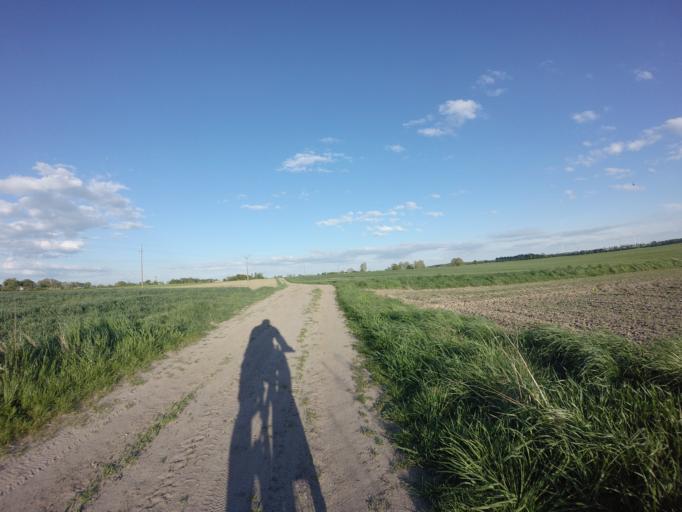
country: PL
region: West Pomeranian Voivodeship
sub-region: Powiat choszczenski
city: Choszczno
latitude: 53.1439
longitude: 15.4246
